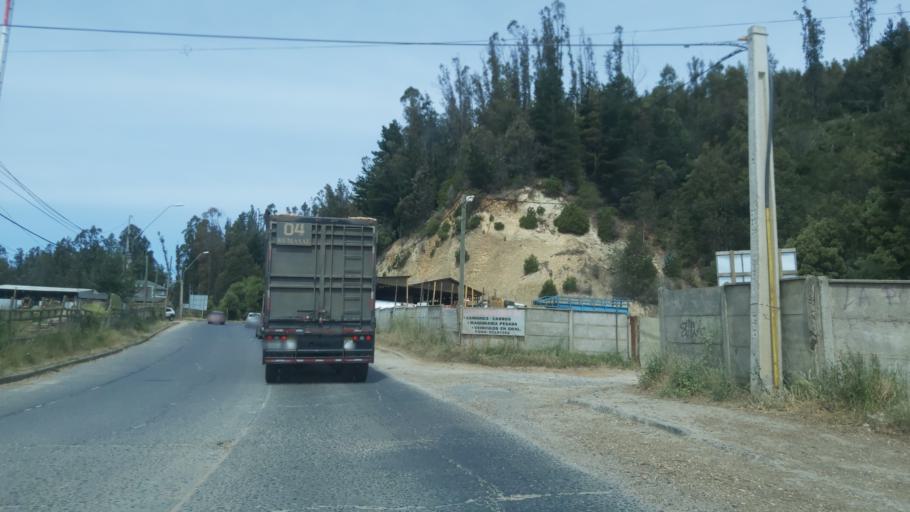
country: CL
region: Maule
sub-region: Provincia de Talca
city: Constitucion
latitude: -35.3460
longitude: -72.4182
